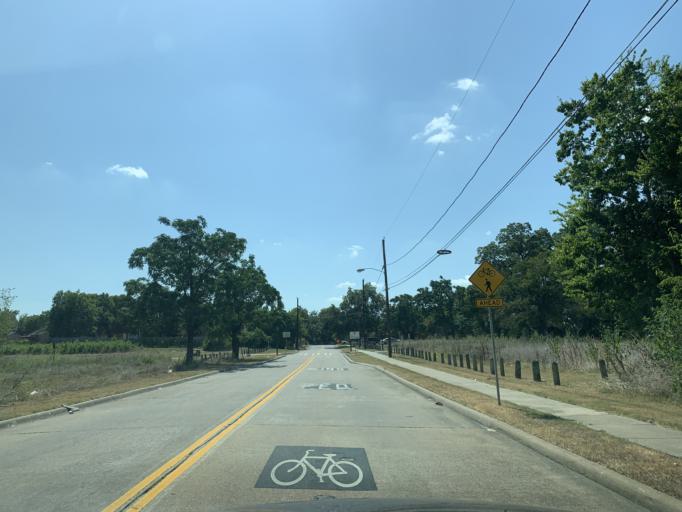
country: US
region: Texas
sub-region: Dallas County
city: Hutchins
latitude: 32.6791
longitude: -96.7921
